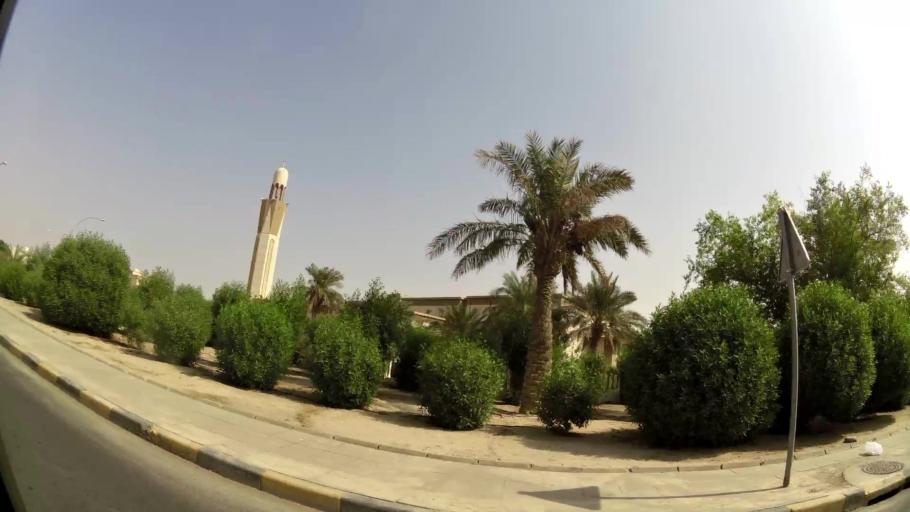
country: KW
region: Muhafazat al Jahra'
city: Al Jahra'
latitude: 29.3301
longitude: 47.6574
